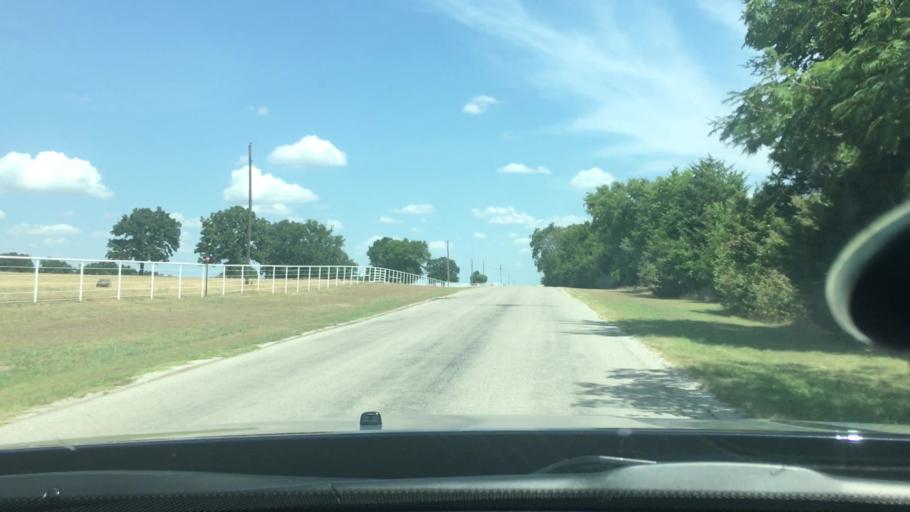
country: US
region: Oklahoma
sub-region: Love County
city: Marietta
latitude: 34.0424
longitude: -97.1957
